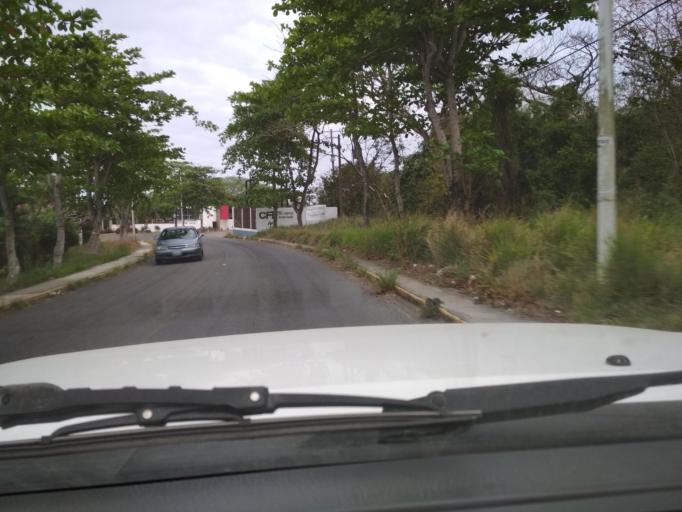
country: MX
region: Veracruz
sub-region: Medellin
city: Fraccionamiento Arboledas San Ramon
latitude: 19.0854
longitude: -96.1521
